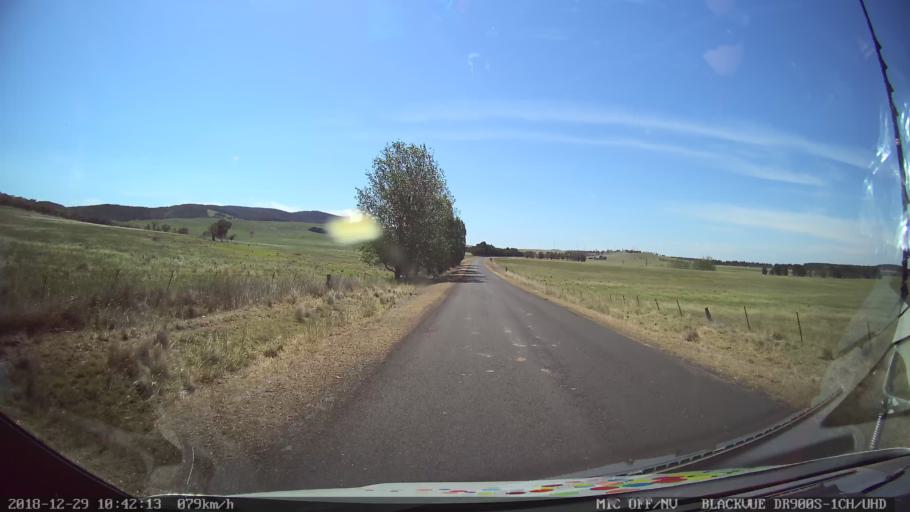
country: AU
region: New South Wales
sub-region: Palerang
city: Bungendore
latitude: -35.0311
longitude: 149.5280
